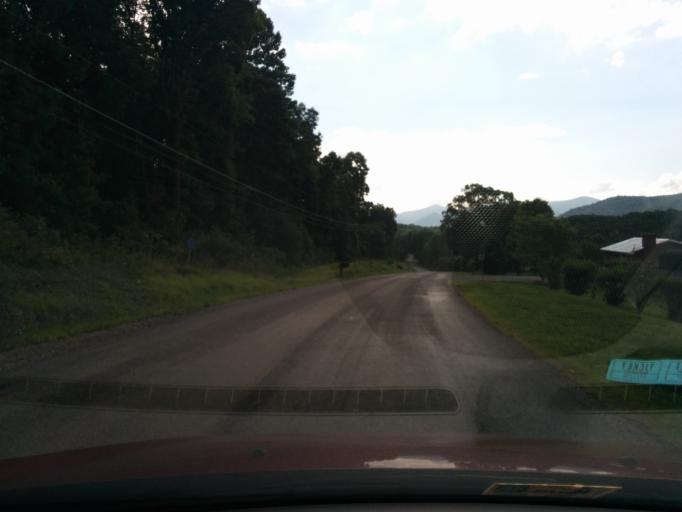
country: US
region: Virginia
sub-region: Rockbridge County
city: Glasgow
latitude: 37.6508
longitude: -79.5202
